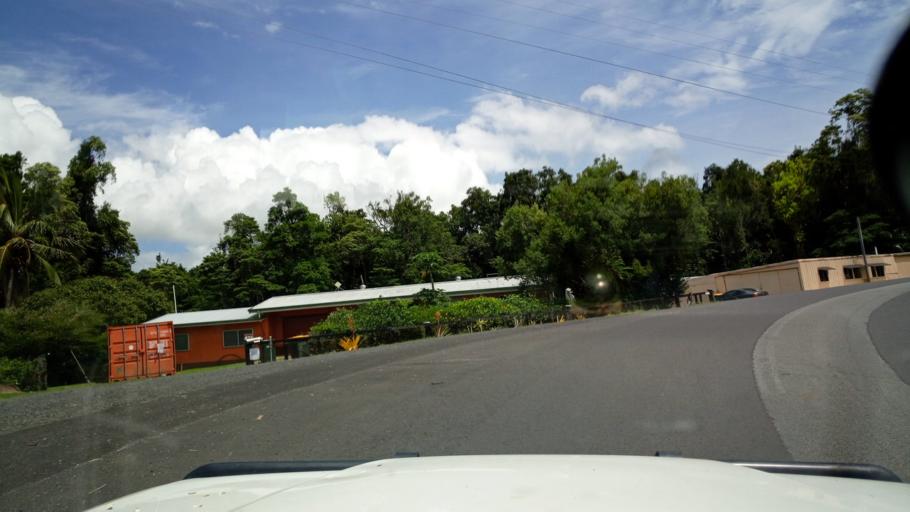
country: AU
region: Queensland
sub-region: Tablelands
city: Kuranda
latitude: -16.8159
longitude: 145.6206
